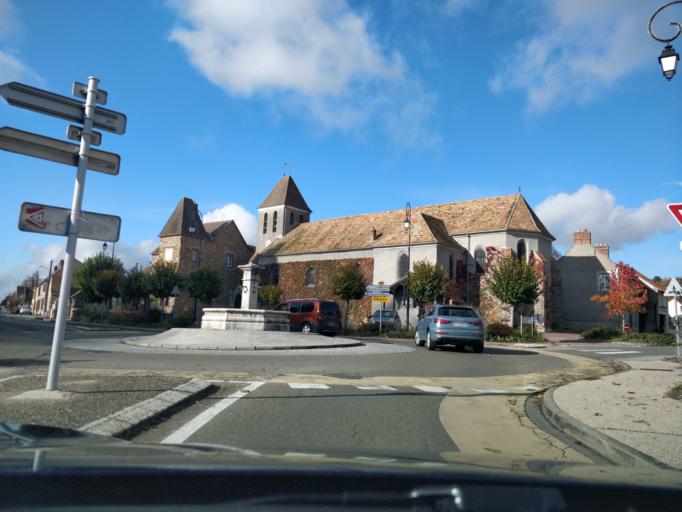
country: FR
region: Ile-de-France
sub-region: Departement de l'Essonne
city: Fontenay-les-Briis
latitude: 48.6190
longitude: 2.1569
